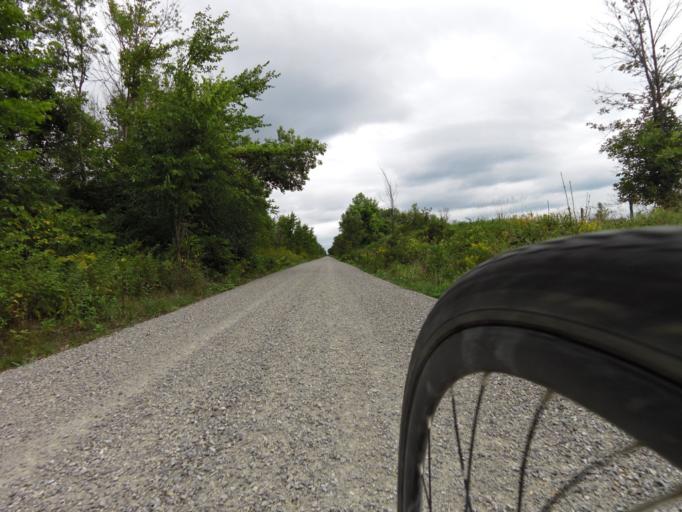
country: CA
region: Ontario
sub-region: Lanark County
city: Smiths Falls
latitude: 44.9293
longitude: -76.0336
